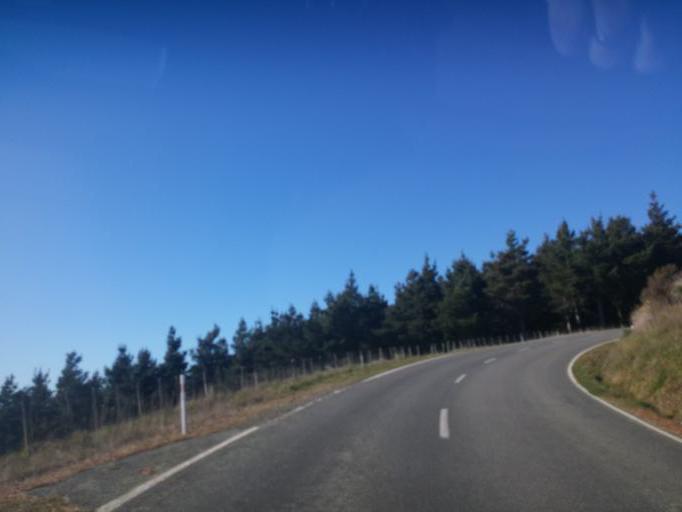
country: NZ
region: Wellington
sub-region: South Wairarapa District
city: Waipawa
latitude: -41.3519
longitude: 175.4945
